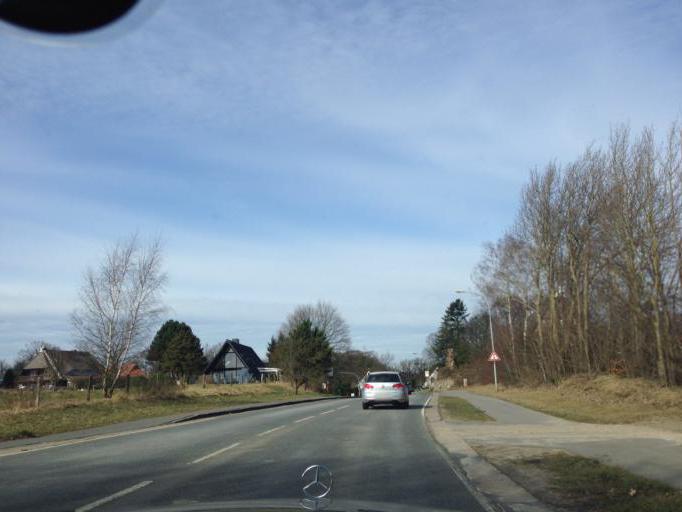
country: DE
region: Lower Saxony
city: Seevetal
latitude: 53.4417
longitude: 9.9048
